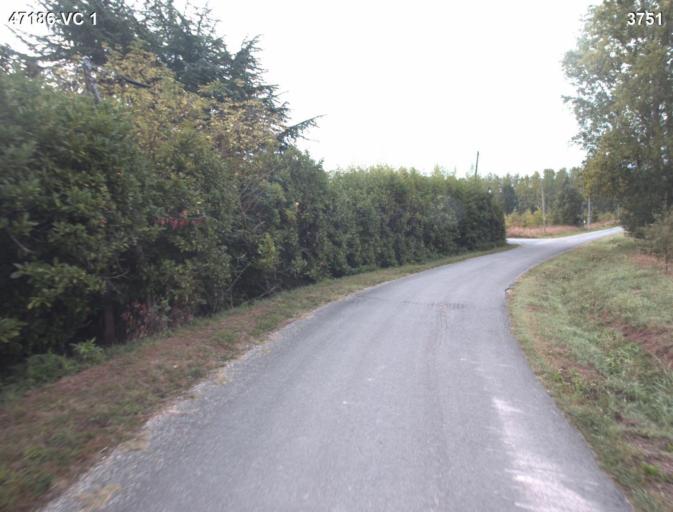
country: FR
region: Aquitaine
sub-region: Departement du Lot-et-Garonne
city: Port-Sainte-Marie
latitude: 44.2196
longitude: 0.4442
